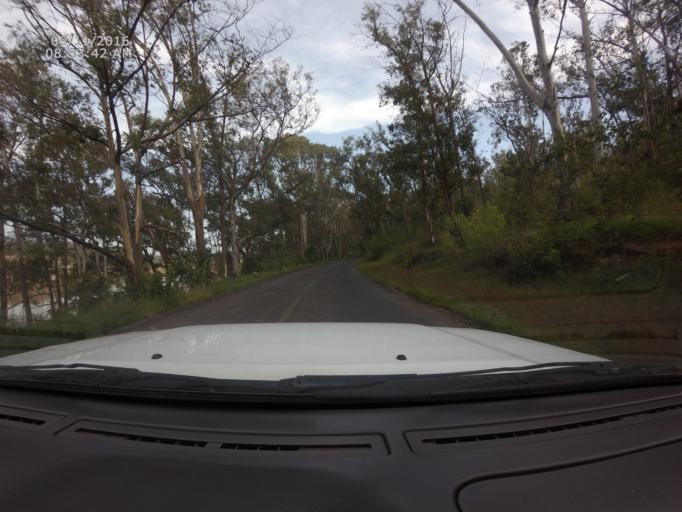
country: MX
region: Michoacan
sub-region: Morelia
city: Morelos
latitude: 19.6288
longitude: -101.2557
